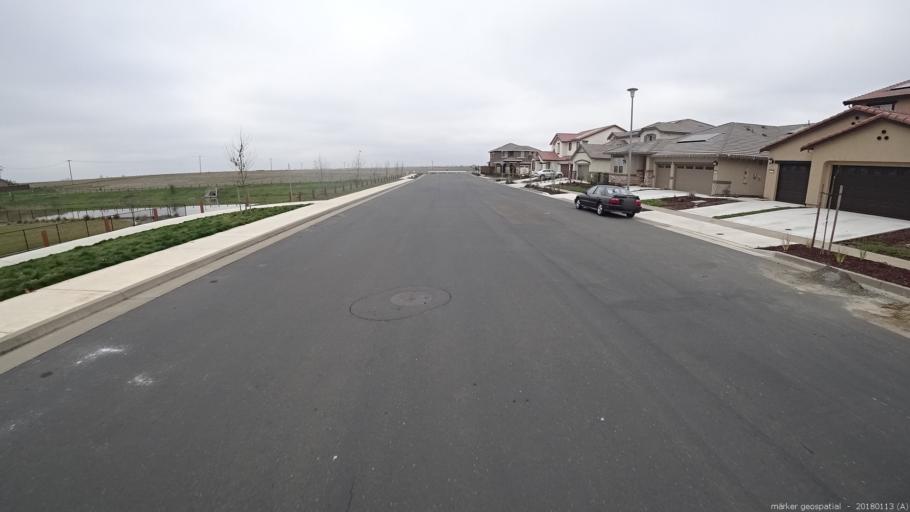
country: US
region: California
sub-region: Sacramento County
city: Gold River
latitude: 38.5701
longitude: -121.2010
